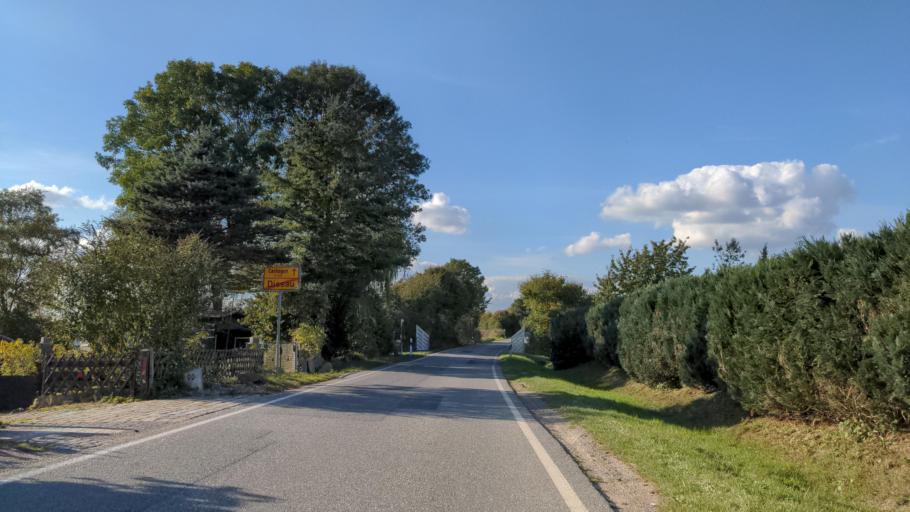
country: DE
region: Schleswig-Holstein
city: Monkhagen
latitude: 53.9421
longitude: 10.5942
